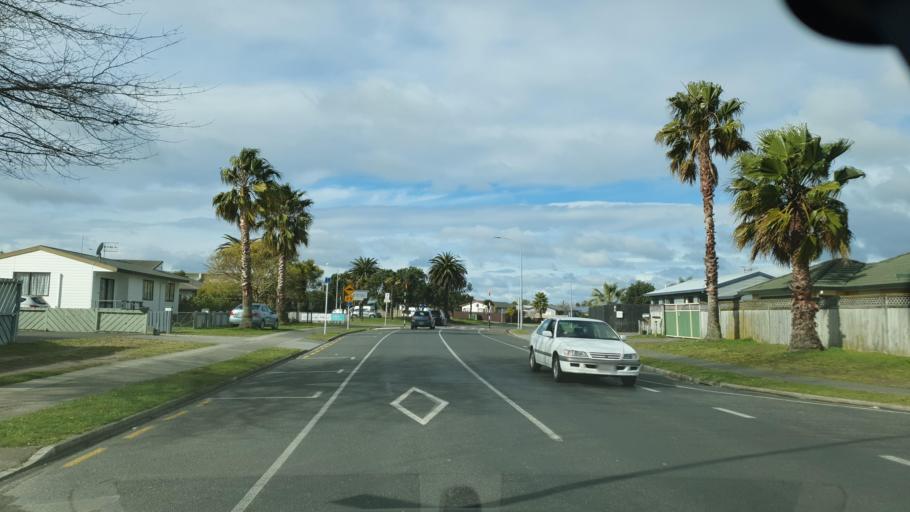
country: NZ
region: Bay of Plenty
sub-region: Tauranga City
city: Tauranga
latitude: -37.7069
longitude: 176.2873
